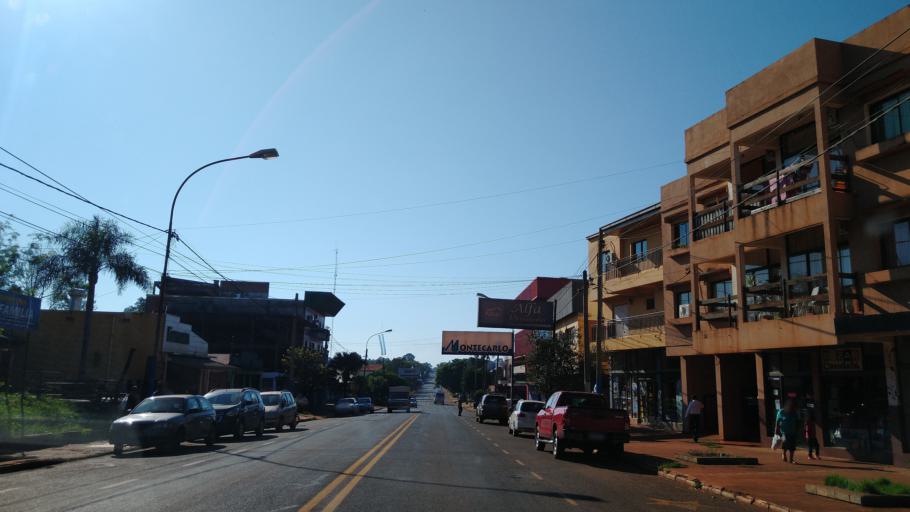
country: AR
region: Misiones
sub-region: Departamento de Montecarlo
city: Montecarlo
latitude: -26.5683
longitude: -54.7588
